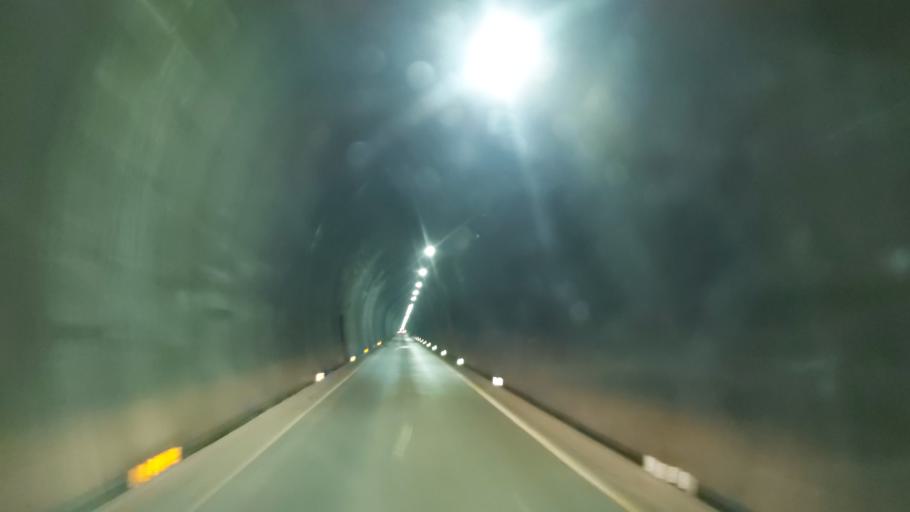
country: CL
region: Araucania
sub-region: Provincia de Cautin
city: Vilcun
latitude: -38.5461
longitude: -71.5037
